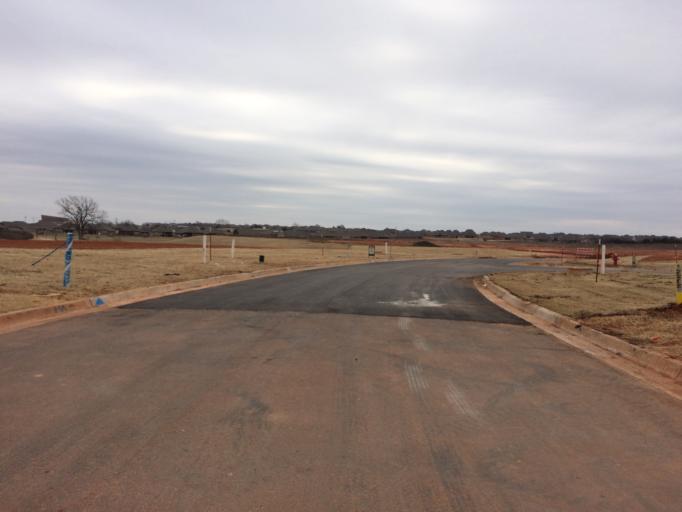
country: US
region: Oklahoma
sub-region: Cleveland County
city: Norman
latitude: 35.2574
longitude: -97.4564
